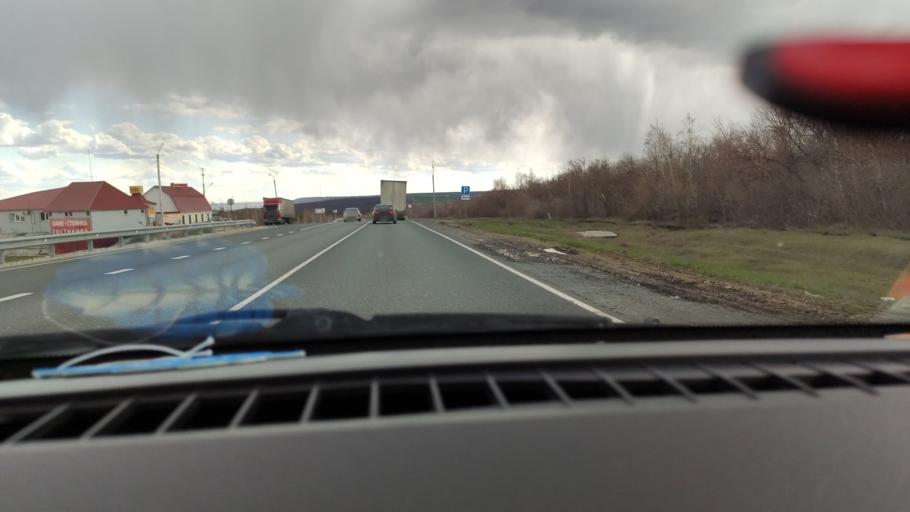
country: RU
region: Saratov
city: Balakovo
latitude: 52.1557
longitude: 47.8162
